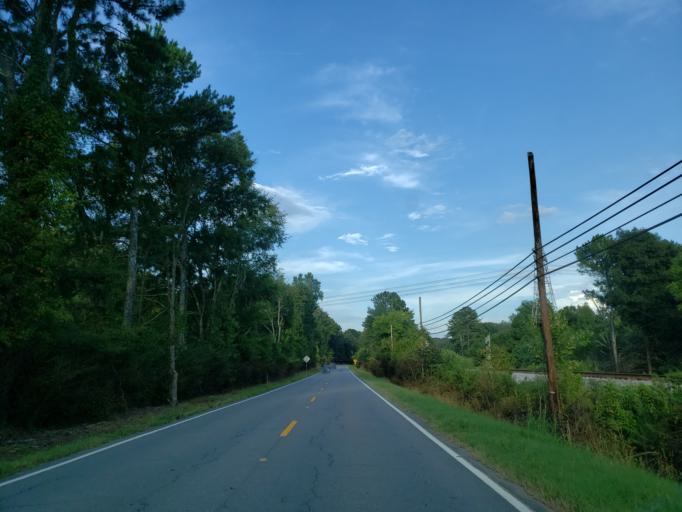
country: US
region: Georgia
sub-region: Bartow County
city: Euharlee
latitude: 34.2381
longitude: -84.9327
